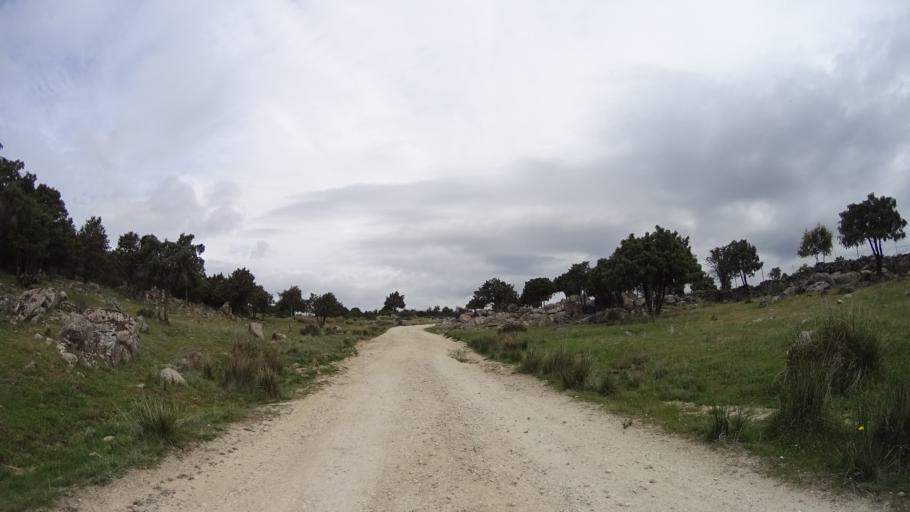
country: ES
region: Madrid
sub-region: Provincia de Madrid
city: Hoyo de Manzanares
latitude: 40.6143
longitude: -3.8793
